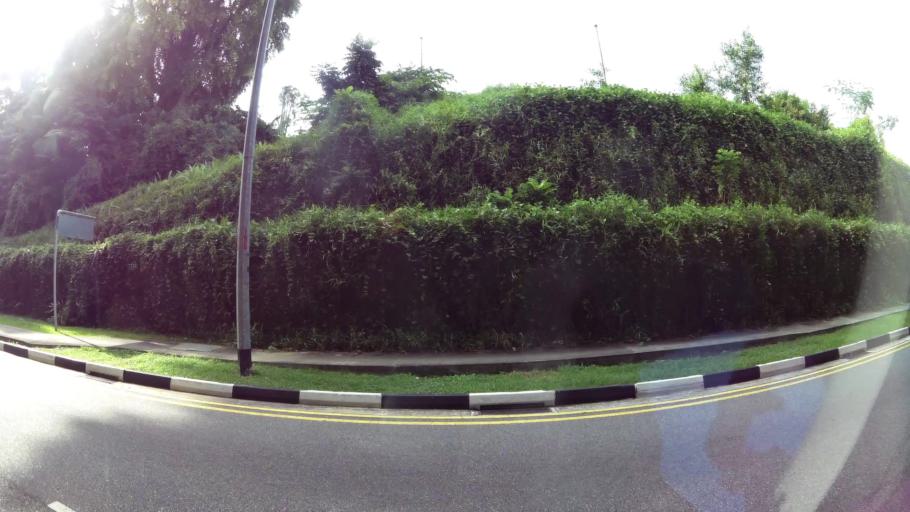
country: SG
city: Singapore
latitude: 1.2724
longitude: 103.8038
